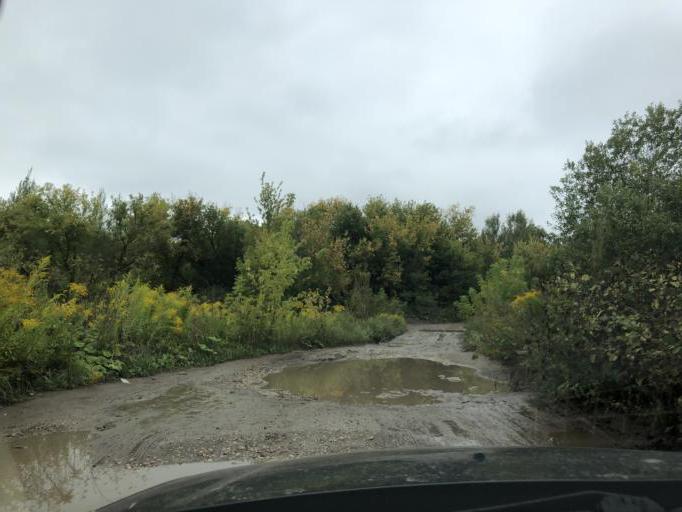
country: RU
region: Tula
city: Mendeleyevskiy
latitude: 54.1685
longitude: 37.5509
